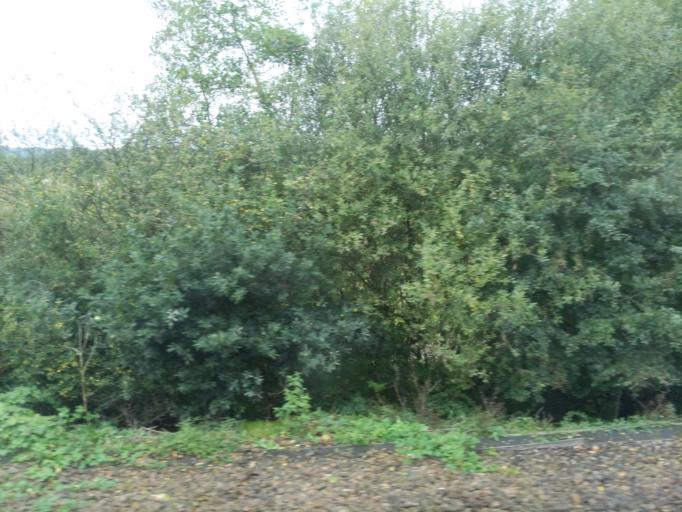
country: GB
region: England
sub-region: Kent
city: Tonbridge
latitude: 51.2029
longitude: 0.2548
